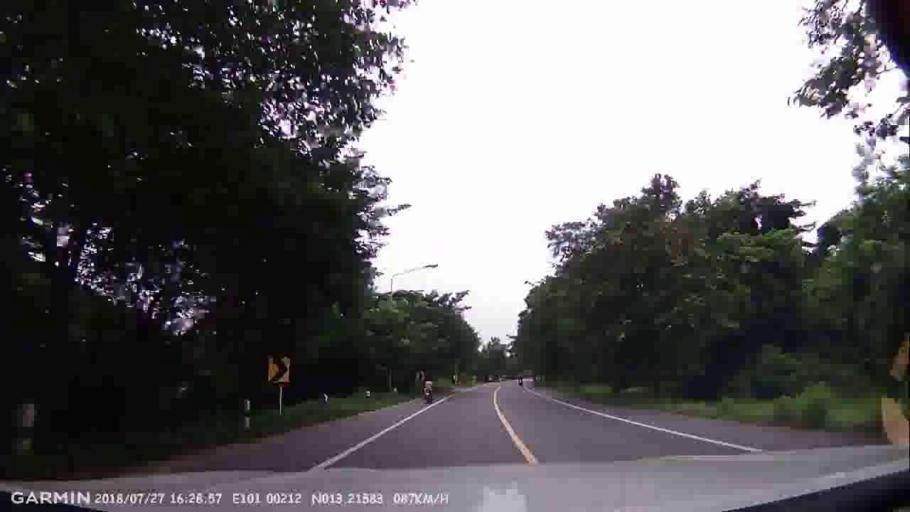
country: TH
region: Chon Buri
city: Si Racha
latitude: 13.2156
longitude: 101.0022
